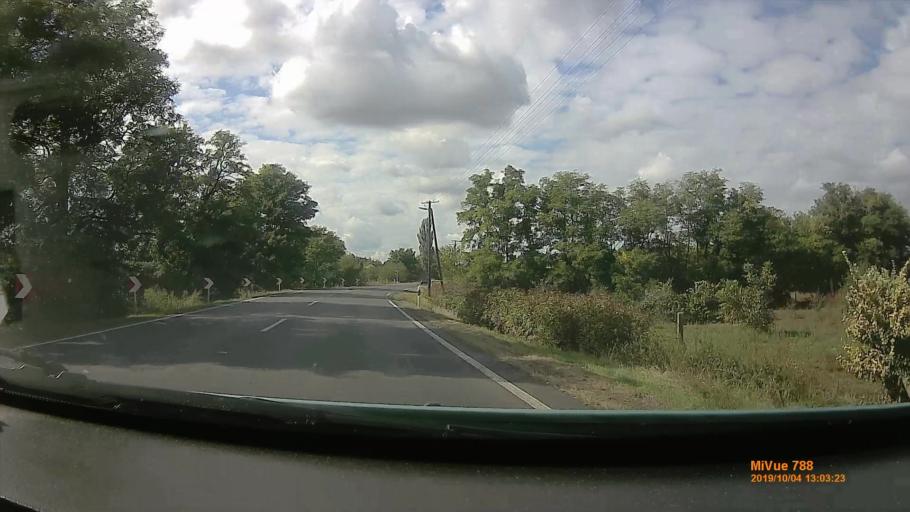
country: HU
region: Szabolcs-Szatmar-Bereg
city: Nyirtelek
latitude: 47.9579
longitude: 21.6351
